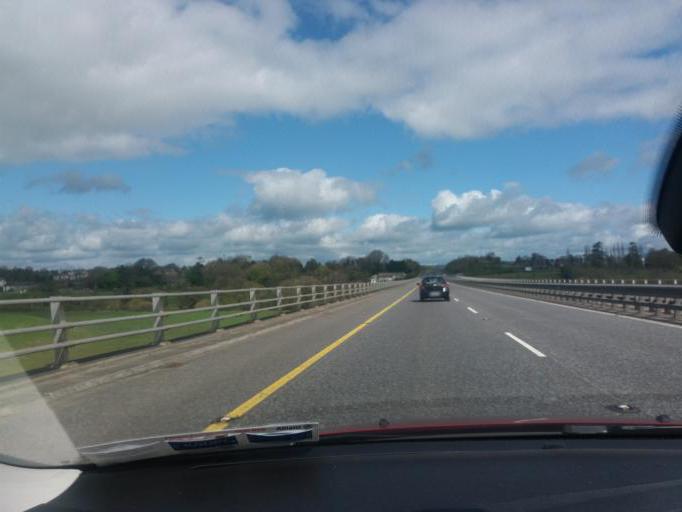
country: IE
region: Munster
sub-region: County Cork
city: Fermoy
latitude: 52.1386
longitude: -8.2616
